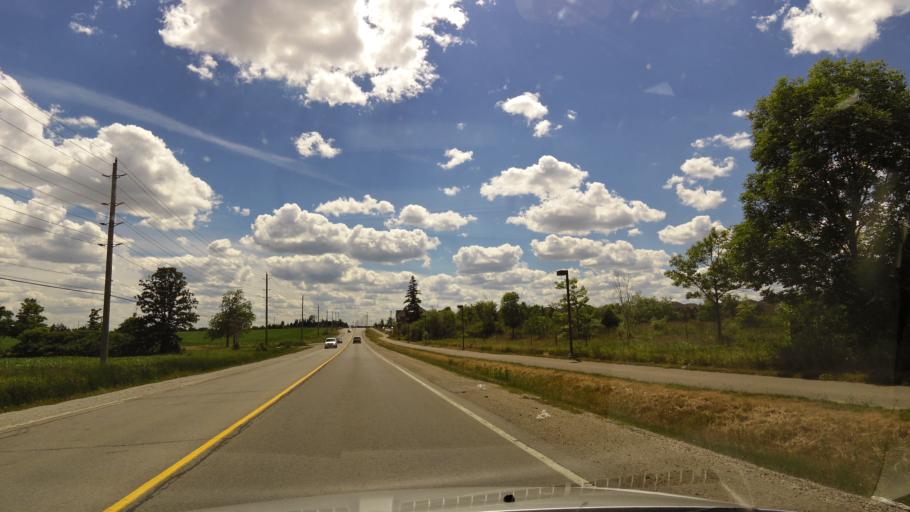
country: CA
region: Ontario
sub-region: Halton
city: Milton
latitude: 43.6215
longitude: -79.8800
